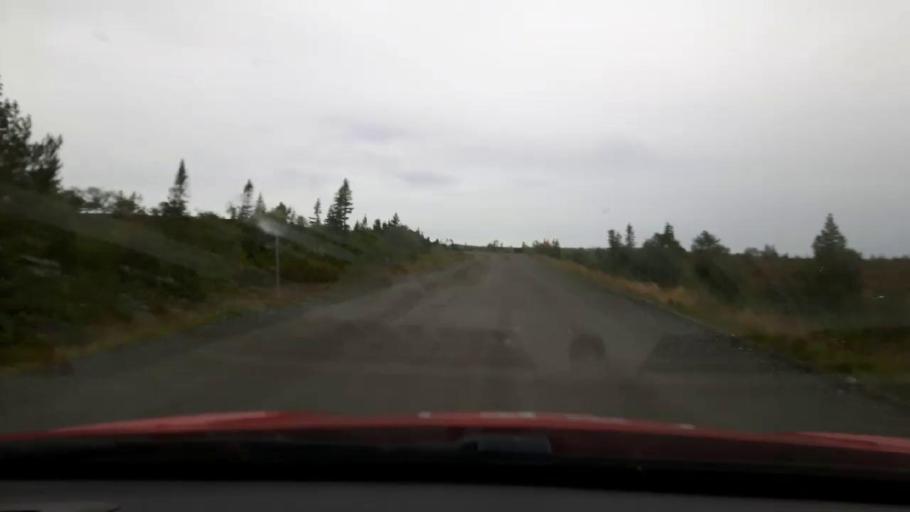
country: NO
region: Nord-Trondelag
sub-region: Meraker
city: Meraker
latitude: 63.6333
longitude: 12.2811
